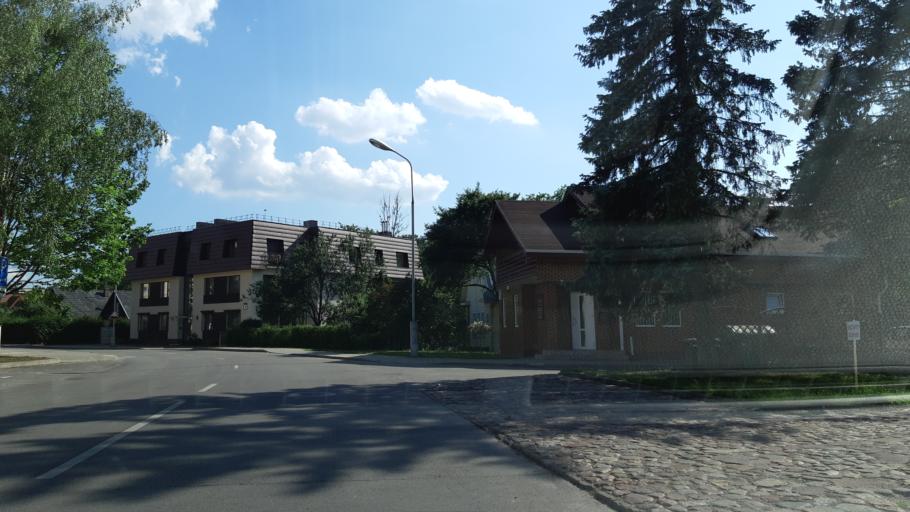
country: LT
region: Alytaus apskritis
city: Druskininkai
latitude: 54.0138
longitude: 23.9817
